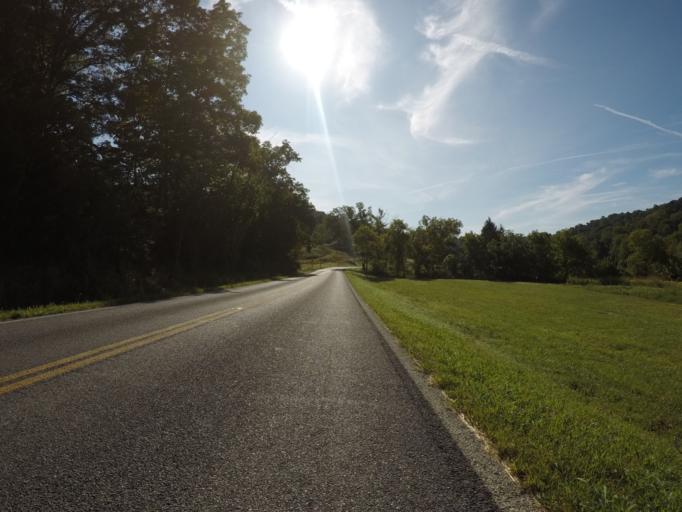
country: US
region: Ohio
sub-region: Lawrence County
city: Burlington
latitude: 38.4984
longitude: -82.5062
